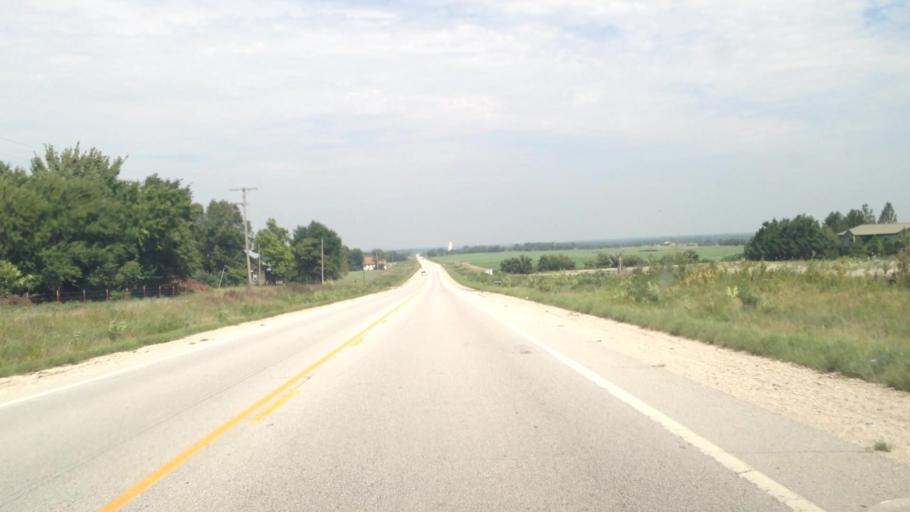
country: US
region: Kansas
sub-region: Neosho County
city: Erie
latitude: 37.4795
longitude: -95.2692
